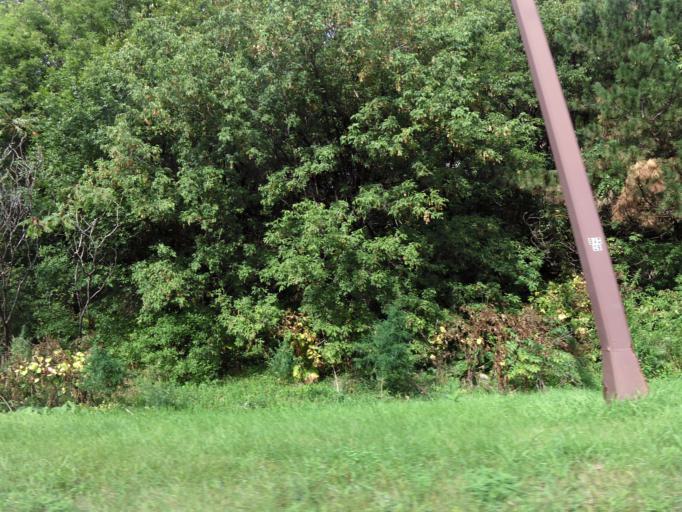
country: US
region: Minnesota
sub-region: Dakota County
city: West Saint Paul
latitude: 44.9288
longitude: -93.1448
